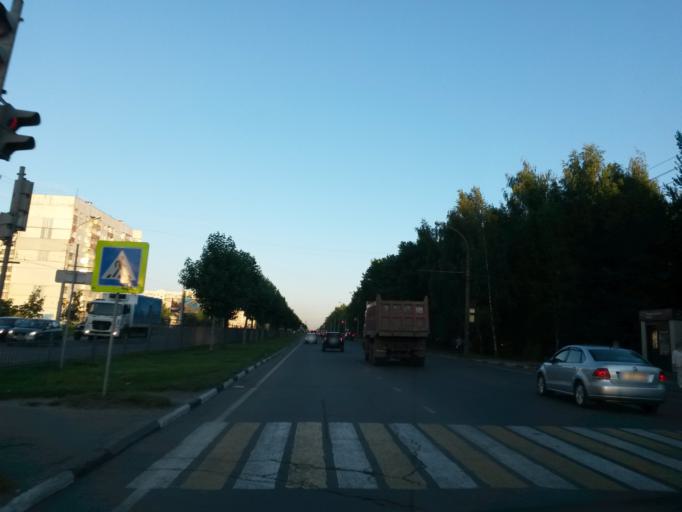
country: RU
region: Jaroslavl
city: Yaroslavl
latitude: 57.6925
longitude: 39.7731
